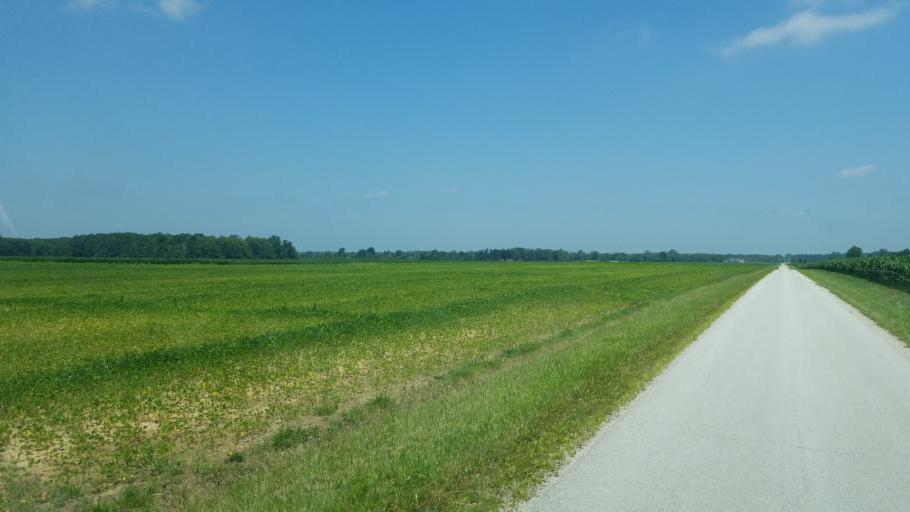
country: US
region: Ohio
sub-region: Sandusky County
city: Green Springs
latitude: 41.0971
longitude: -82.9767
